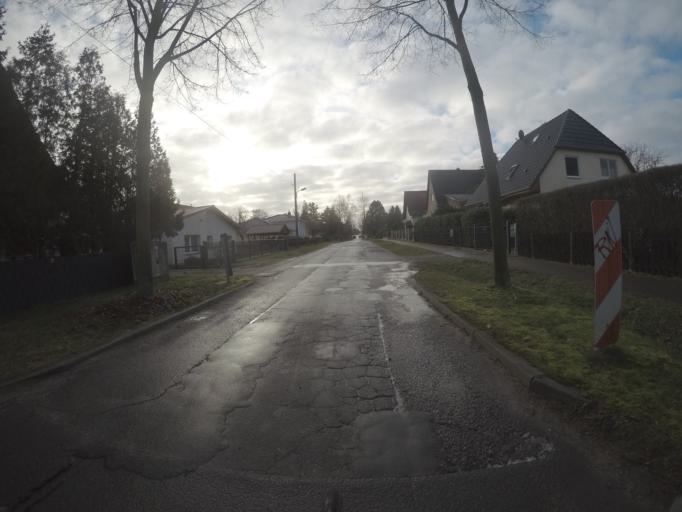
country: DE
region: Berlin
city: Falkenberg
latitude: 52.5771
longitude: 13.5597
